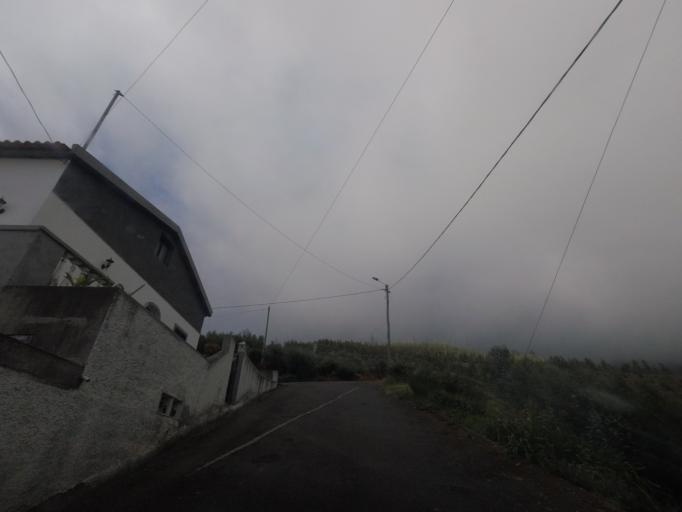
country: PT
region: Madeira
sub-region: Funchal
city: Nossa Senhora do Monte
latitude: 32.6824
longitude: -16.9084
